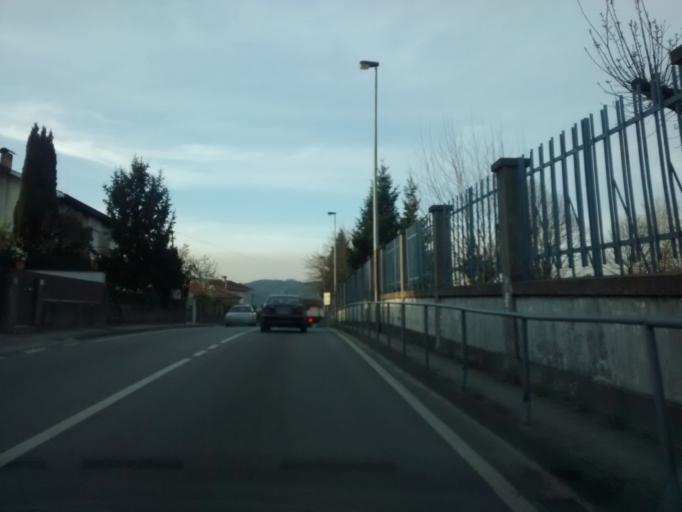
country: PT
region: Braga
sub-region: Guimaraes
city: Brito
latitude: 41.4838
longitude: -8.3533
